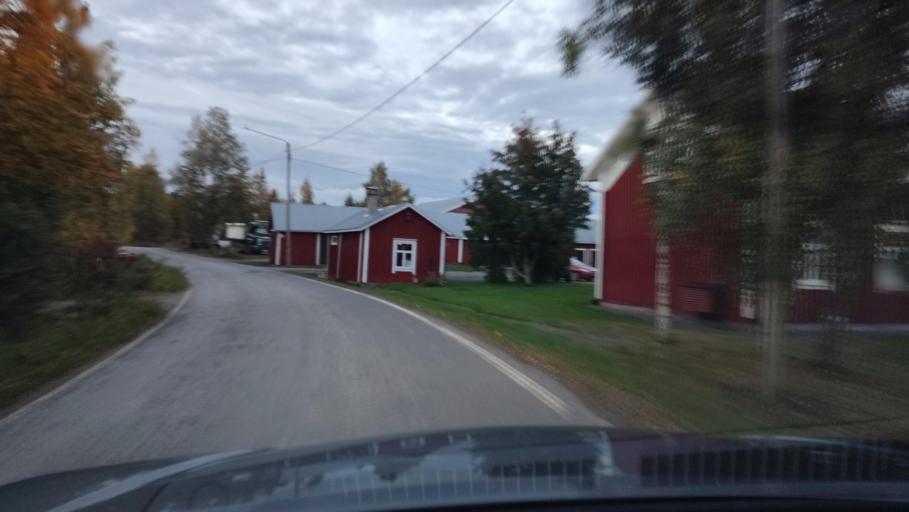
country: FI
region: Ostrobothnia
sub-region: Sydosterbotten
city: Kristinestad
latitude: 62.2648
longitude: 21.5095
